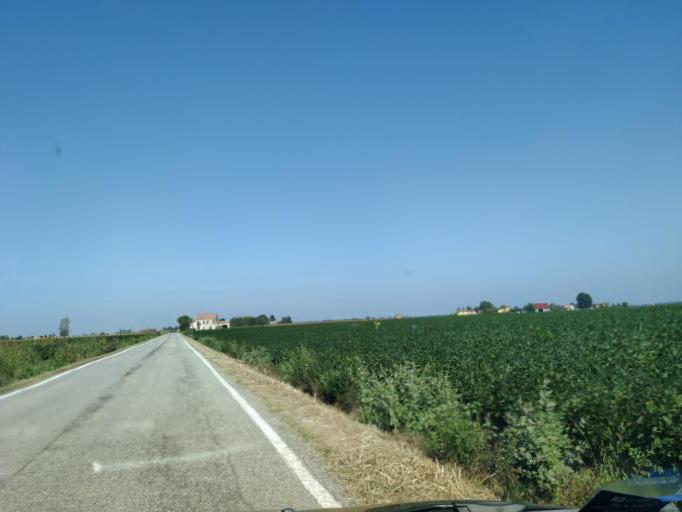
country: IT
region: Emilia-Romagna
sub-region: Provincia di Ferrara
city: Coccanile-Cesta
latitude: 44.9058
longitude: 11.8979
